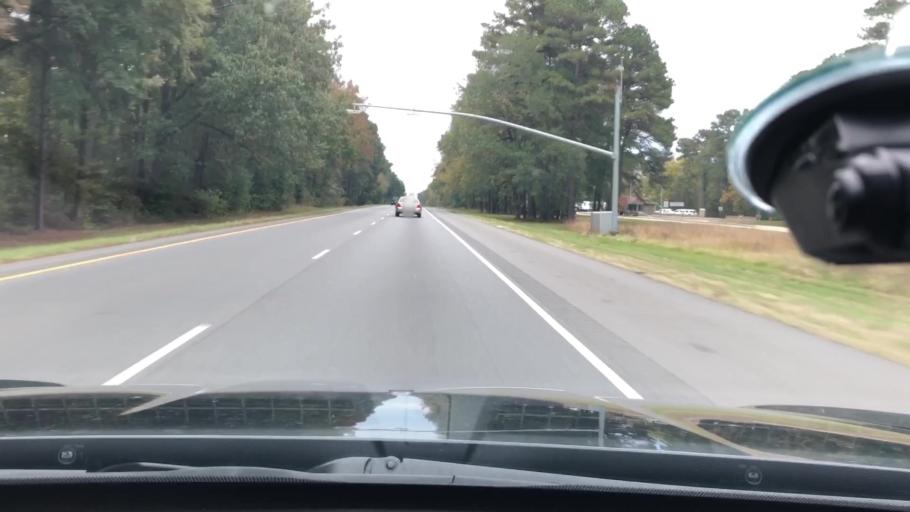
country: US
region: Arkansas
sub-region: Hempstead County
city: Hope
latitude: 33.6493
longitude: -93.6734
